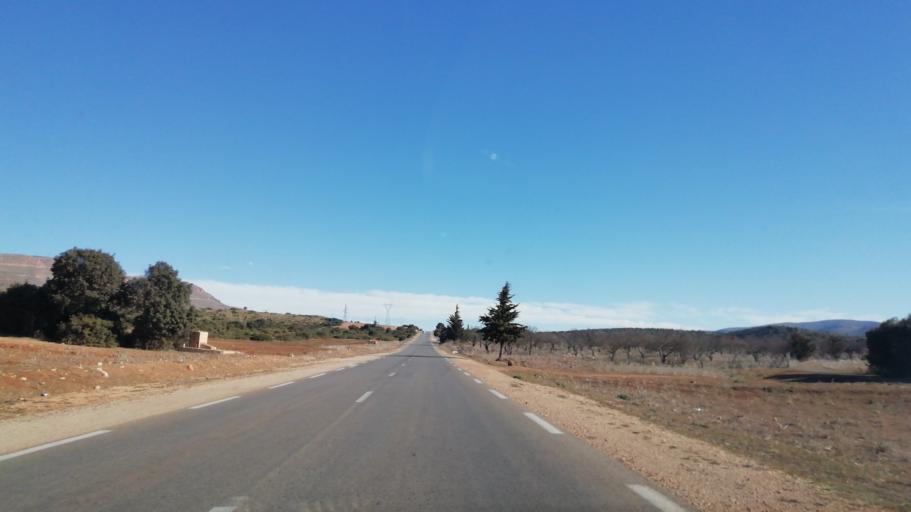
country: DZ
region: Tlemcen
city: Sebdou
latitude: 34.7090
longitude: -1.2134
